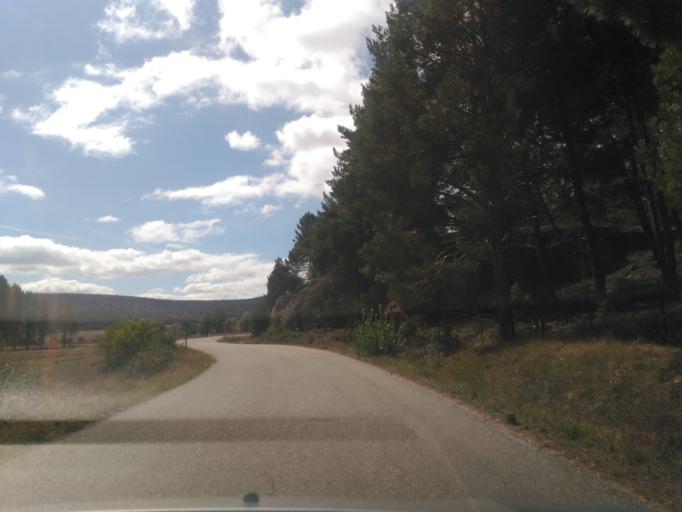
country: ES
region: Castille and Leon
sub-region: Provincia de Burgos
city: Rabanera del Pinar
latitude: 41.8578
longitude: -3.1972
